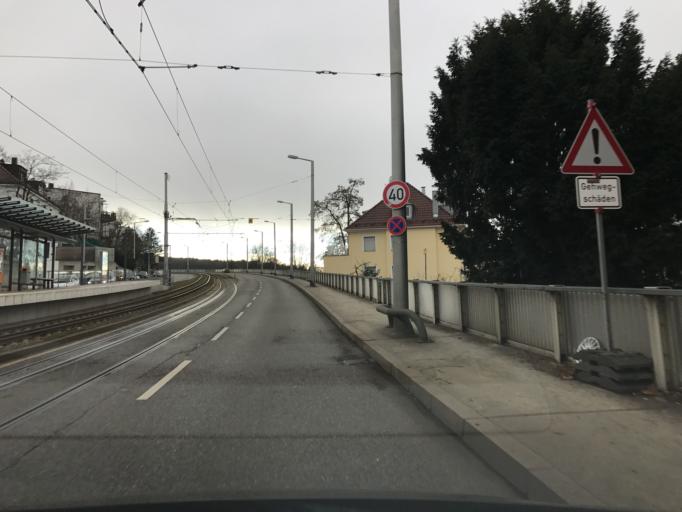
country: DE
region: Baden-Wuerttemberg
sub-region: Regierungsbezirk Stuttgart
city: Stuttgart-Ost
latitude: 48.7696
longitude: 9.1955
